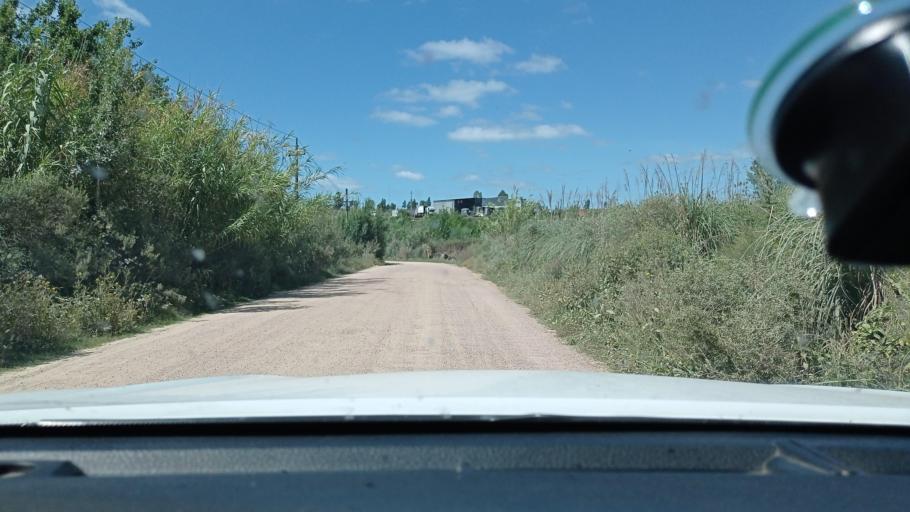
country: UY
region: Canelones
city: Pando
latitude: -34.7243
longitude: -55.9737
